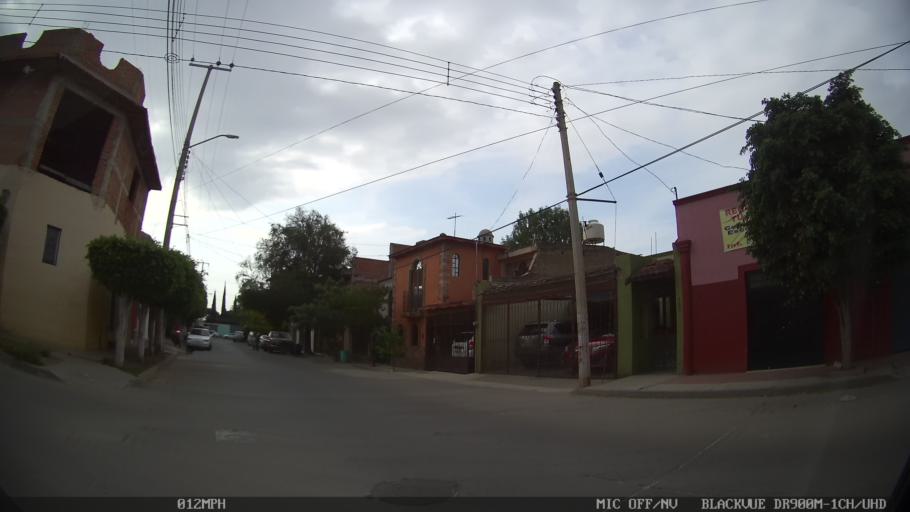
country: MX
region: Jalisco
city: Tonala
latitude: 20.6300
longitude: -103.2358
